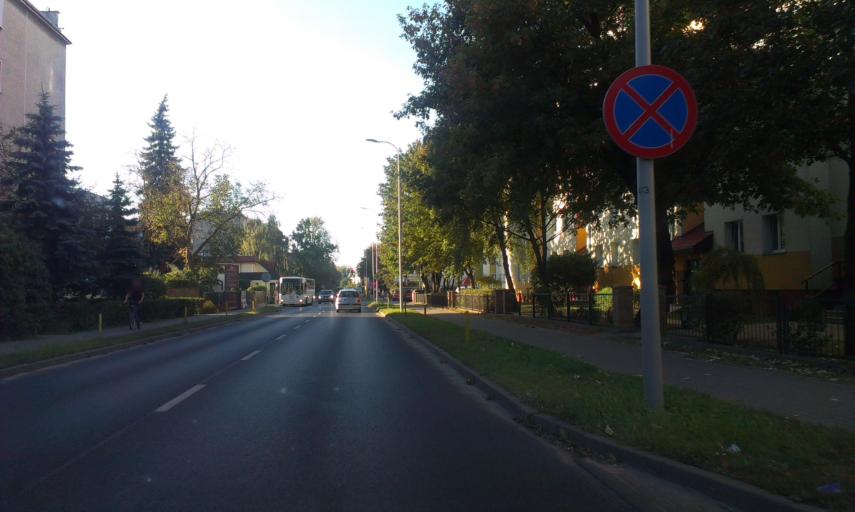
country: PL
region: Kujawsko-Pomorskie
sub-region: Torun
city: Torun
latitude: 53.0242
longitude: 18.6015
